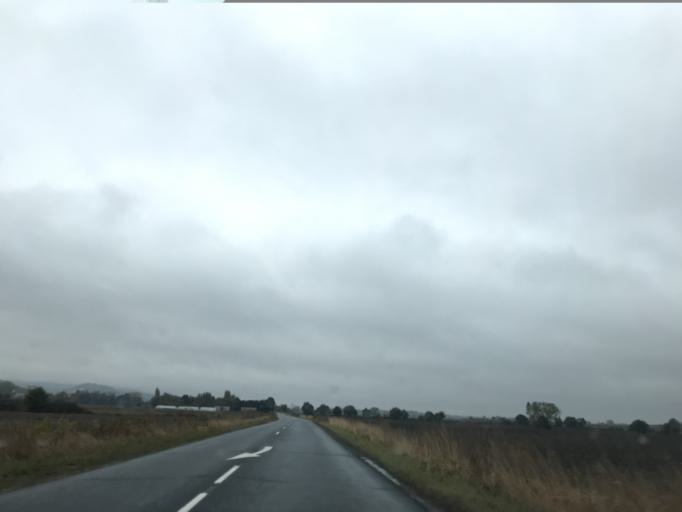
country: FR
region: Auvergne
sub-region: Departement du Puy-de-Dome
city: Vertaizon
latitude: 45.7802
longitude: 3.3398
